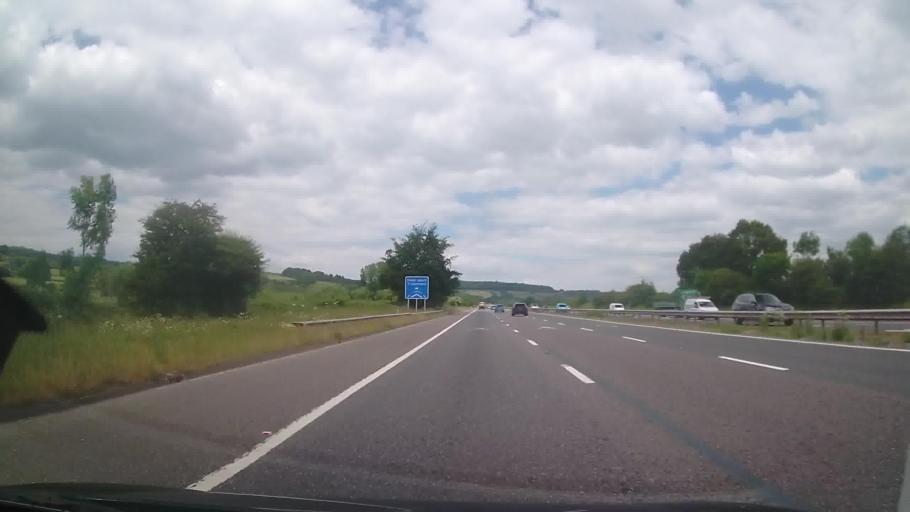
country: GB
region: England
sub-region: North Somerset
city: Banwell
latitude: 51.3009
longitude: -2.8909
